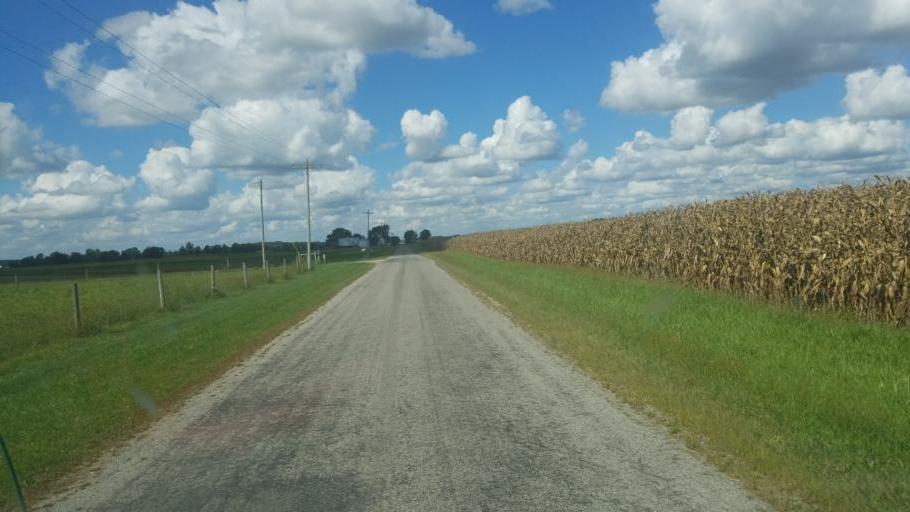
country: US
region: Ohio
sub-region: Union County
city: Richwood
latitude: 40.4453
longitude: -83.4929
